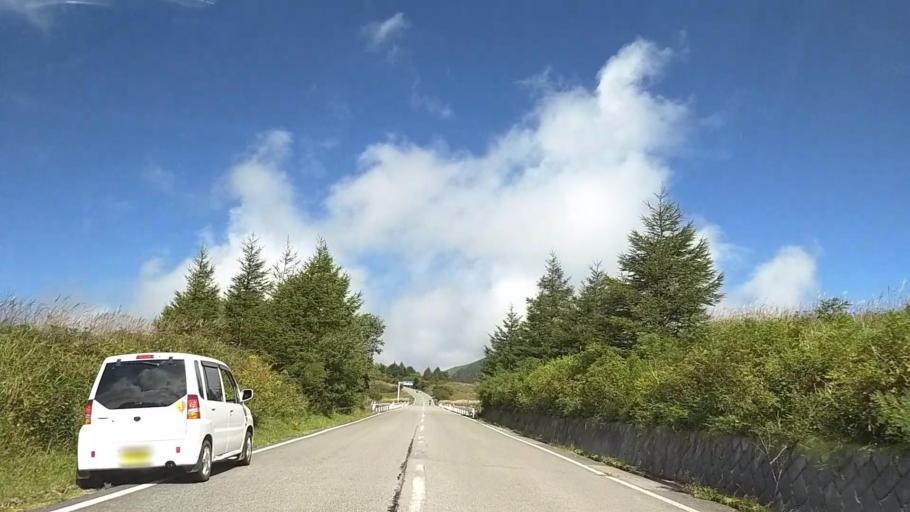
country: JP
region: Nagano
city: Suwa
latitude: 36.1133
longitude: 138.1650
